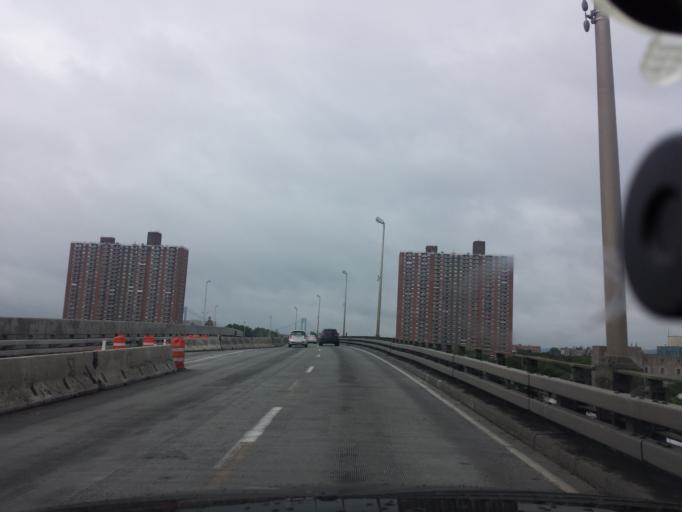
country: US
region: New York
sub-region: Kings County
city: Bensonhurst
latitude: 40.6425
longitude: -74.0204
